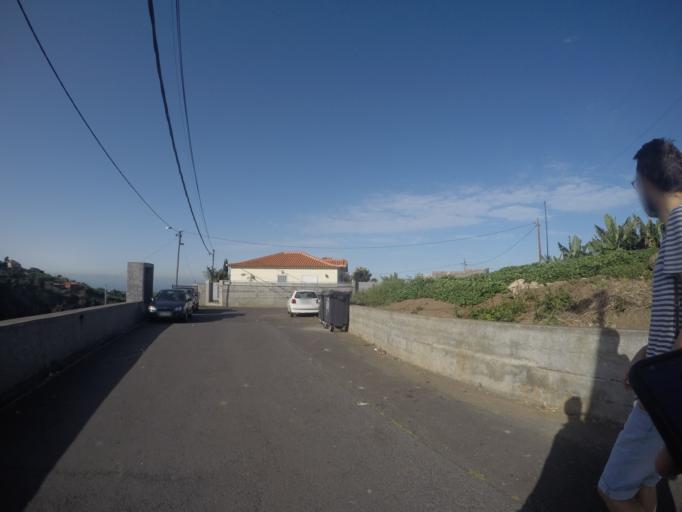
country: PT
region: Madeira
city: Camara de Lobos
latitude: 32.6656
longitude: -16.9568
